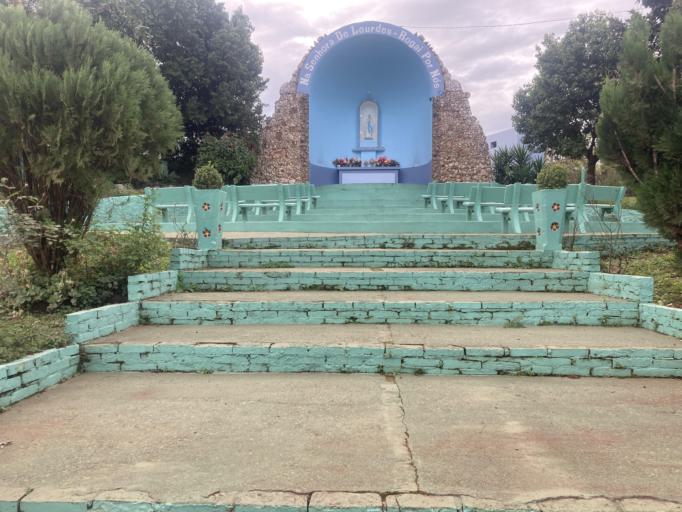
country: BR
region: Rio Grande do Sul
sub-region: Sao Pedro Do Butia
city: Butia Inferior
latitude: -27.9818
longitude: -54.8588
